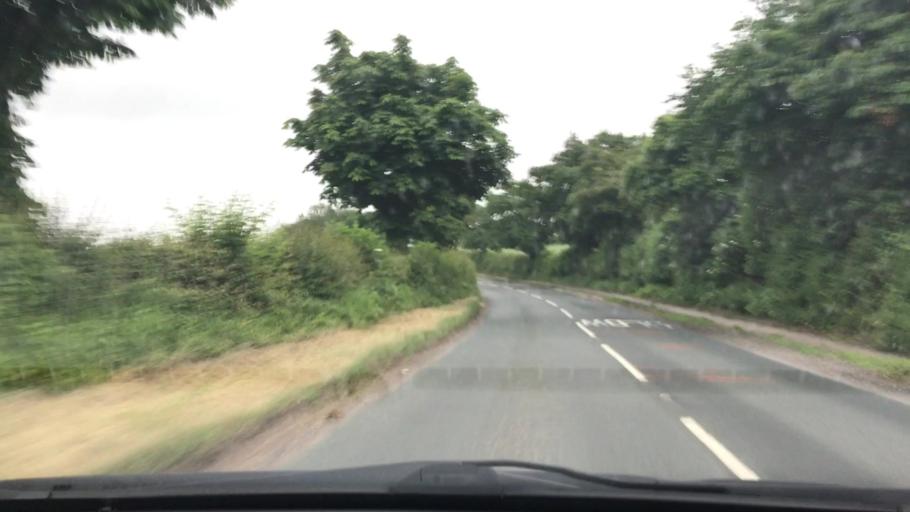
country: GB
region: England
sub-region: City and Borough of Leeds
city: Wetherby
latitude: 53.9579
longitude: -1.4038
